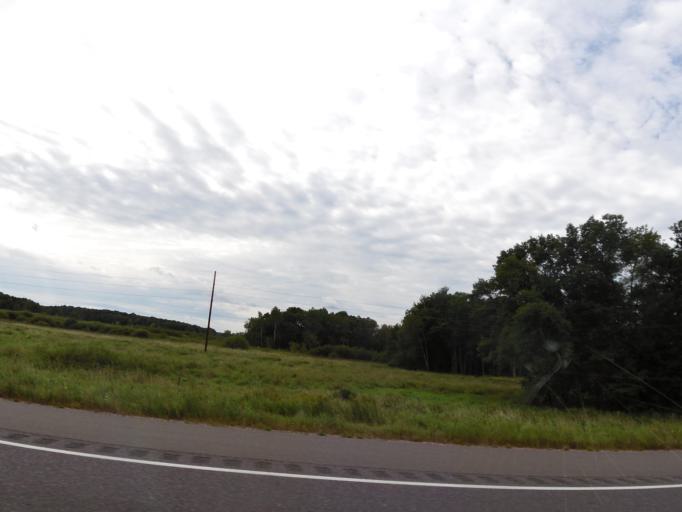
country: US
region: Wisconsin
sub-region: Juneau County
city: Mauston
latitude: 43.7444
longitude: -89.9417
